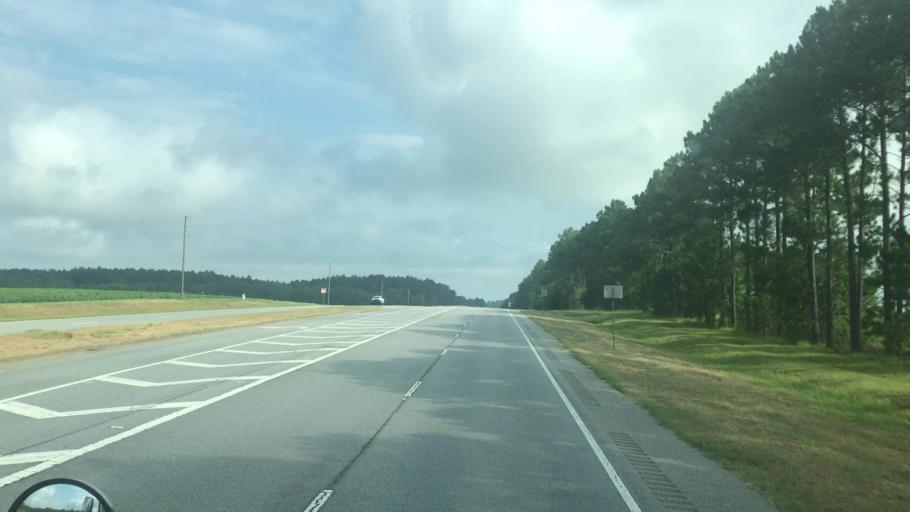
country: US
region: Georgia
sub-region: Miller County
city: Colquitt
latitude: 31.1912
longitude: -84.7651
